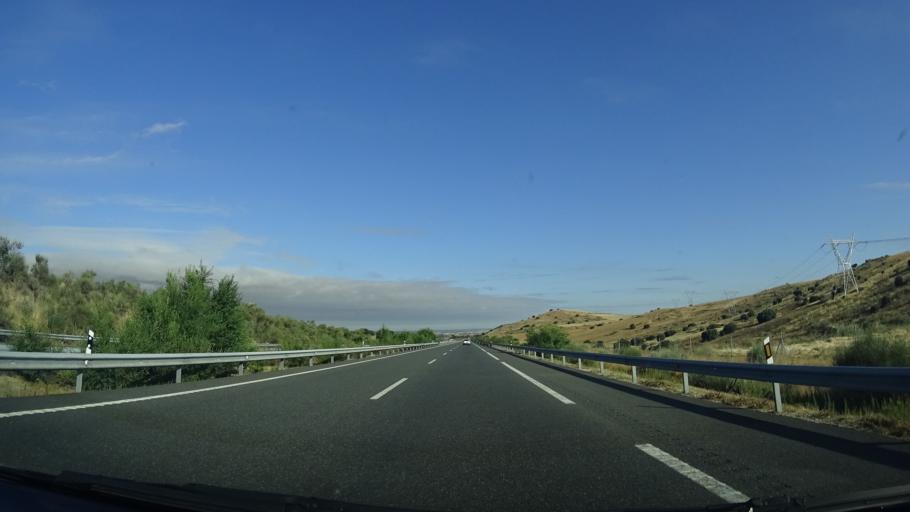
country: ES
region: Castille and Leon
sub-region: Provincia de Segovia
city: Labajos
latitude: 40.8341
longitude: -4.5284
